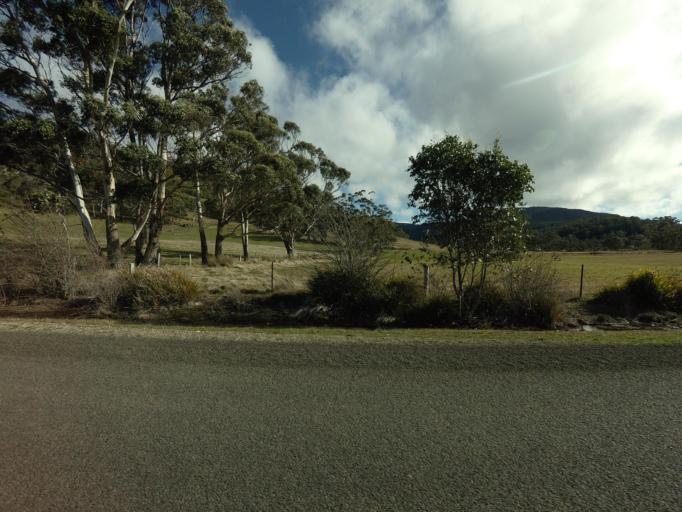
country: AU
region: Tasmania
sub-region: Derwent Valley
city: New Norfolk
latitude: -42.6077
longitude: 146.7057
